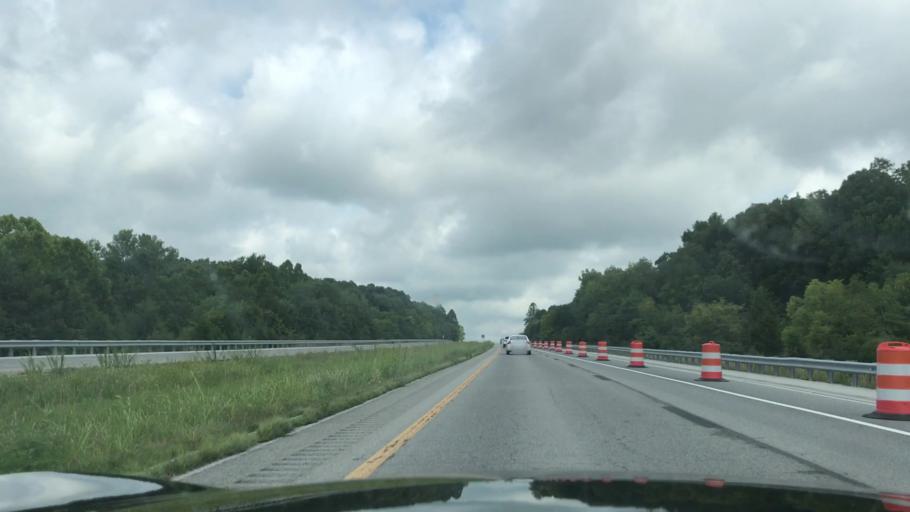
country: US
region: Kentucky
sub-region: Butler County
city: Morgantown
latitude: 37.0935
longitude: -86.6297
